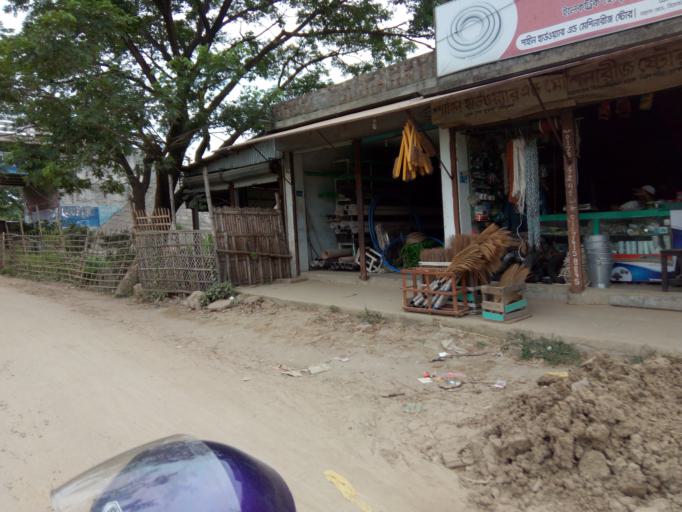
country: BD
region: Dhaka
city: Paltan
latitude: 23.7531
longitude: 90.4524
